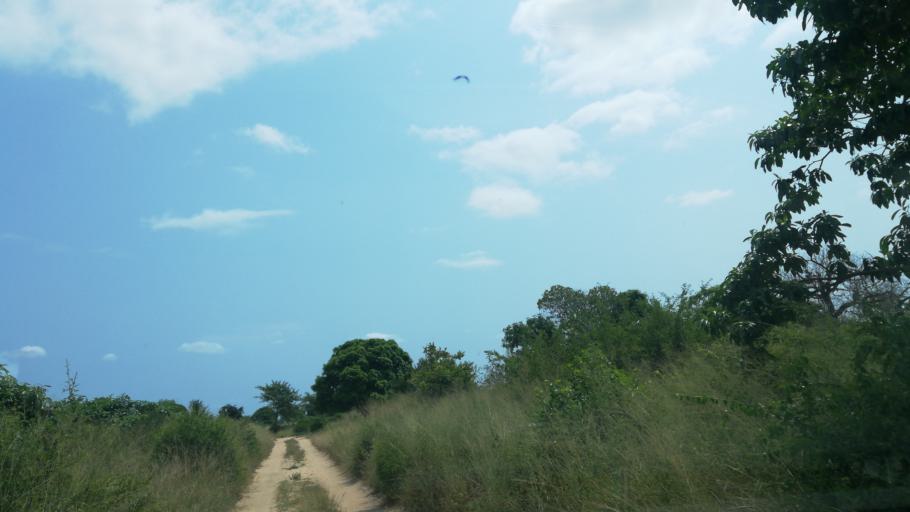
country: MZ
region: Maputo
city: Matola
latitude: -26.1102
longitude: 32.4182
